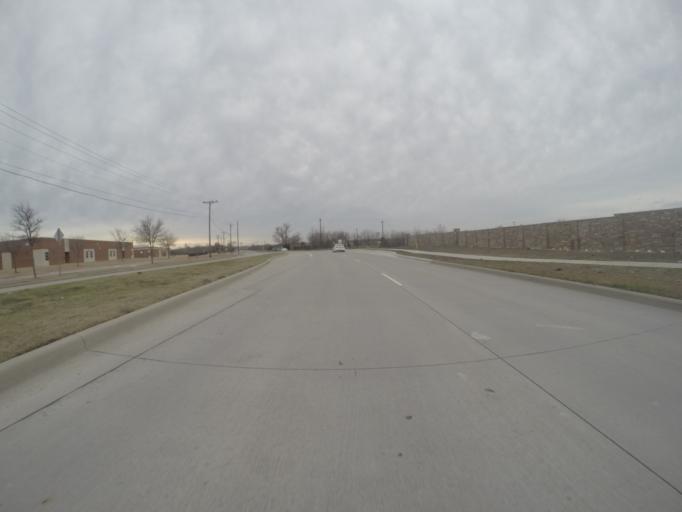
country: US
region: Texas
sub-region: Collin County
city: Saint Paul
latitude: 33.0283
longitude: -96.5686
